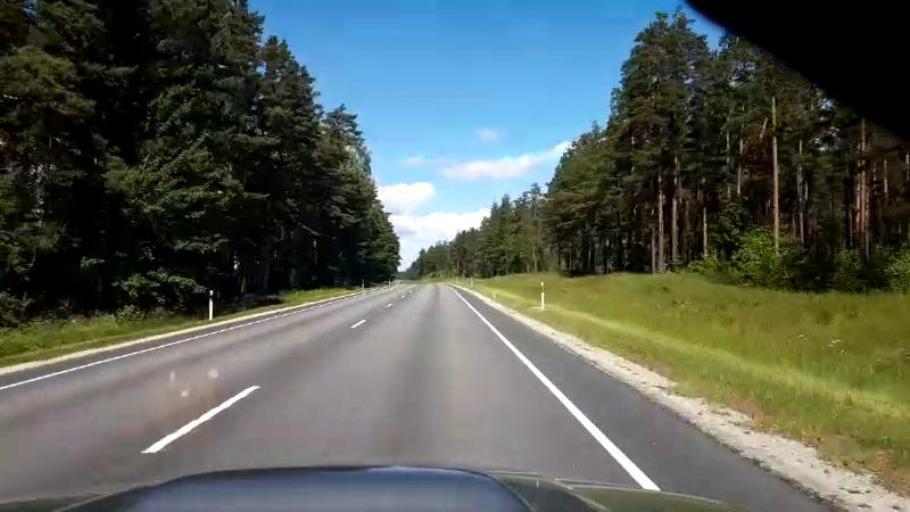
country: EE
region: Paernumaa
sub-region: Paernu linn
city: Parnu
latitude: 58.1647
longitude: 24.4971
